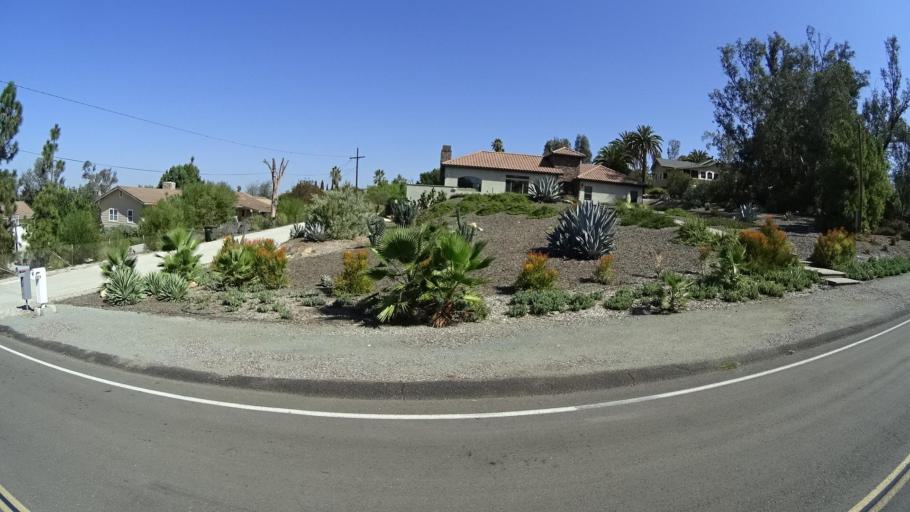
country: US
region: California
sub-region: San Diego County
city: Granite Hills
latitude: 32.7914
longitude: -116.9081
